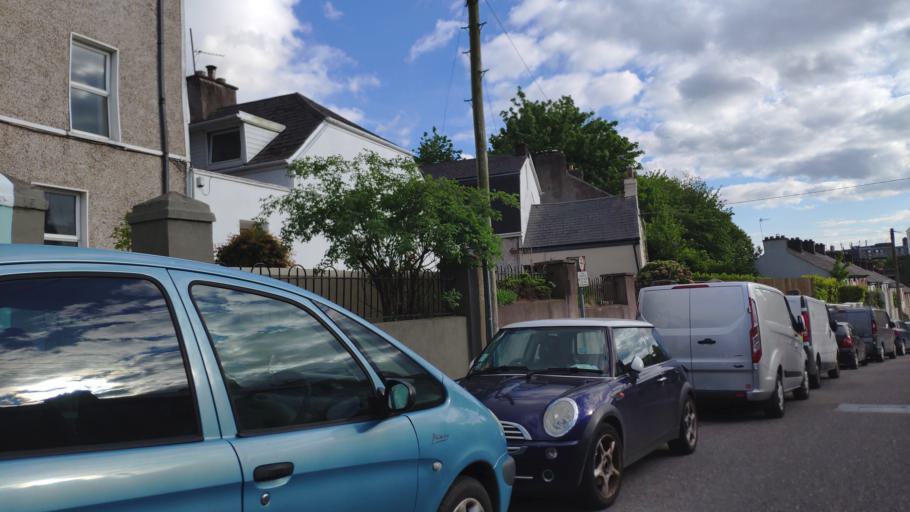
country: IE
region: Munster
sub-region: County Cork
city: Cork
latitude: 51.9077
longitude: -8.4563
